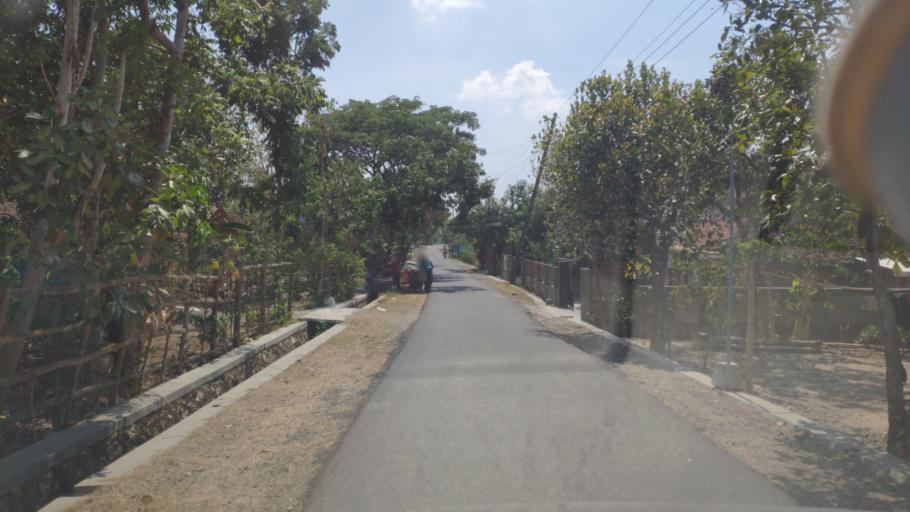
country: ID
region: Central Java
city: Kembang
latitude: -6.9982
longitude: 111.3496
